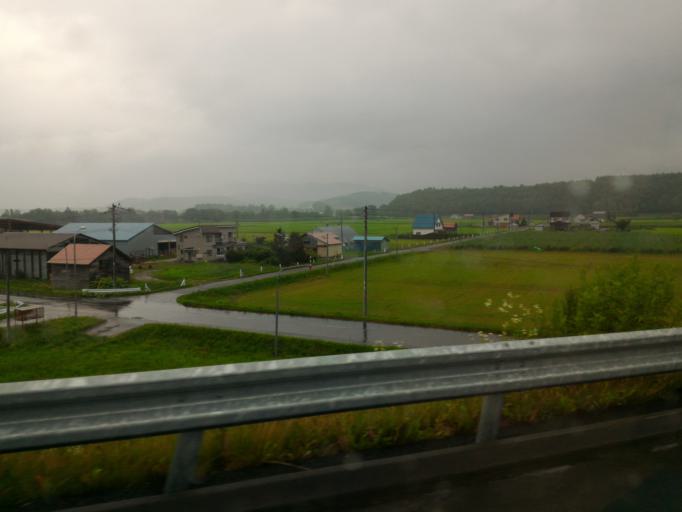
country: JP
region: Hokkaido
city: Nayoro
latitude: 44.4946
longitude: 142.3470
